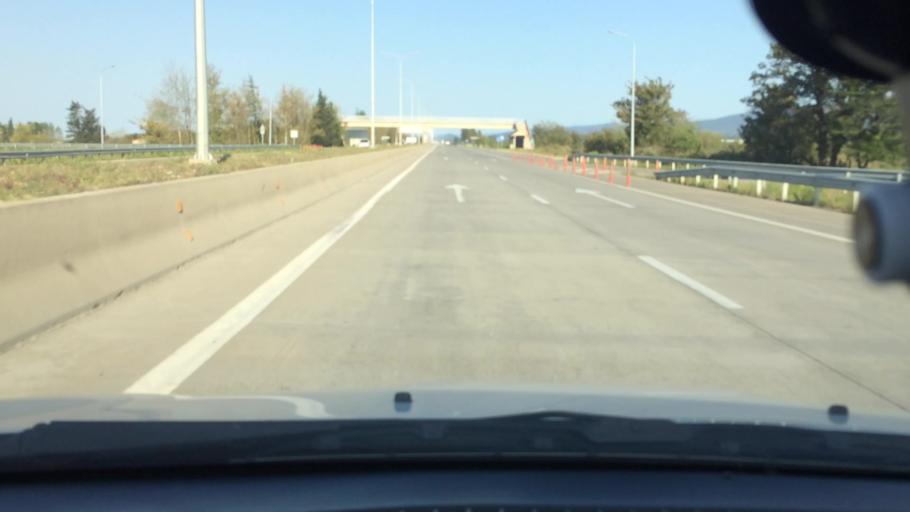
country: GE
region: Imereti
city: Zestap'oni
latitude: 42.1596
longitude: 42.9492
